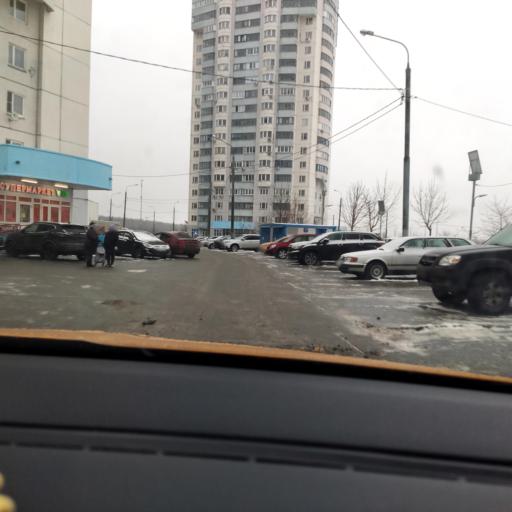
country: RU
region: Moscow
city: Nekrasovka
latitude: 55.7220
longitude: 37.9082
